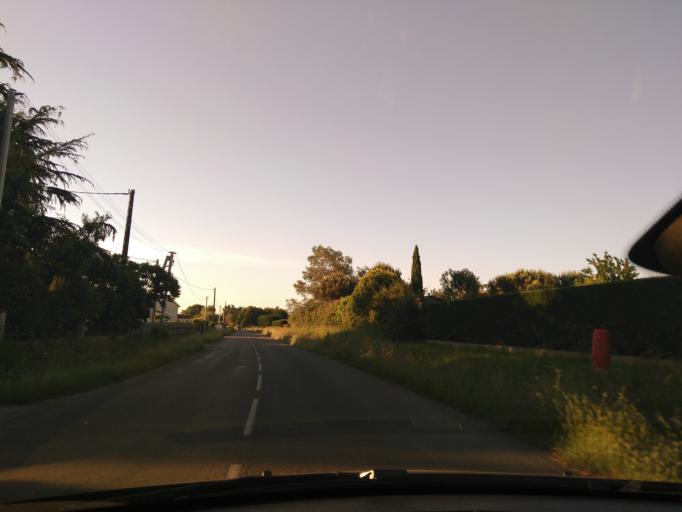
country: FR
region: Midi-Pyrenees
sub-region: Departement de la Haute-Garonne
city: Merville
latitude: 43.7162
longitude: 1.3056
